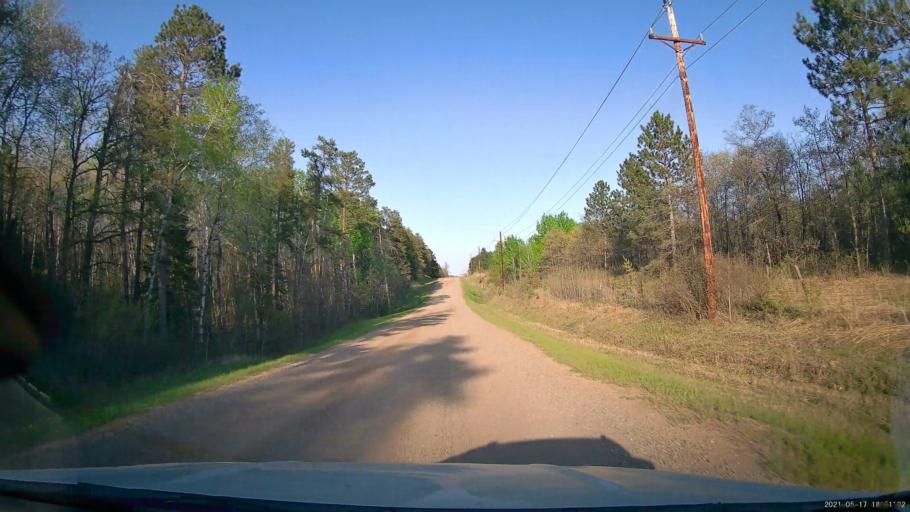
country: US
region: Minnesota
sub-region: Hubbard County
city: Park Rapids
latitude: 46.9437
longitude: -95.0114
